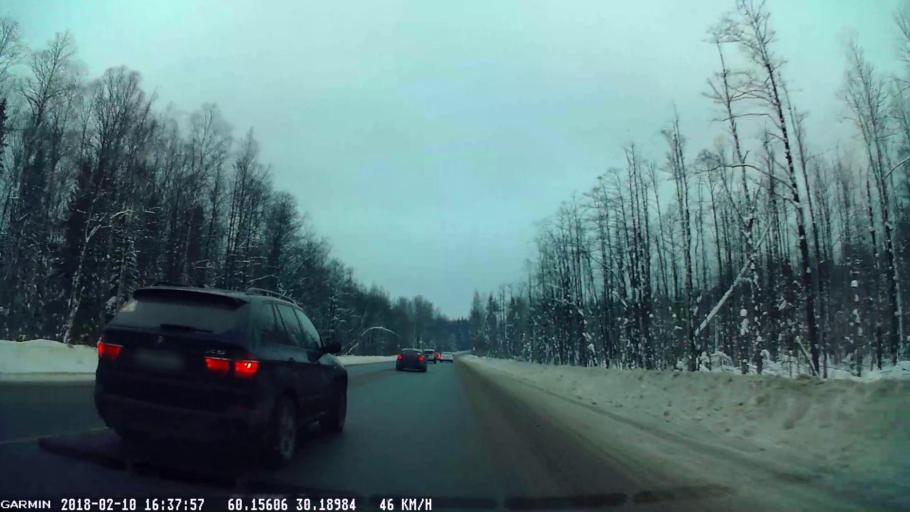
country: RU
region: Leningrad
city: Sertolovo
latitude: 60.1522
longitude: 30.1948
